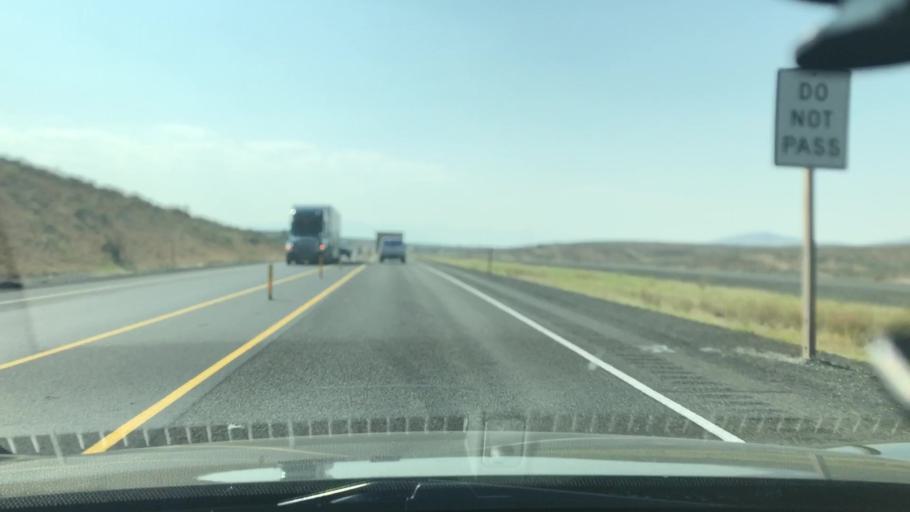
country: US
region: Oregon
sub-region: Baker County
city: Baker City
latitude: 44.6853
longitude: -117.6680
